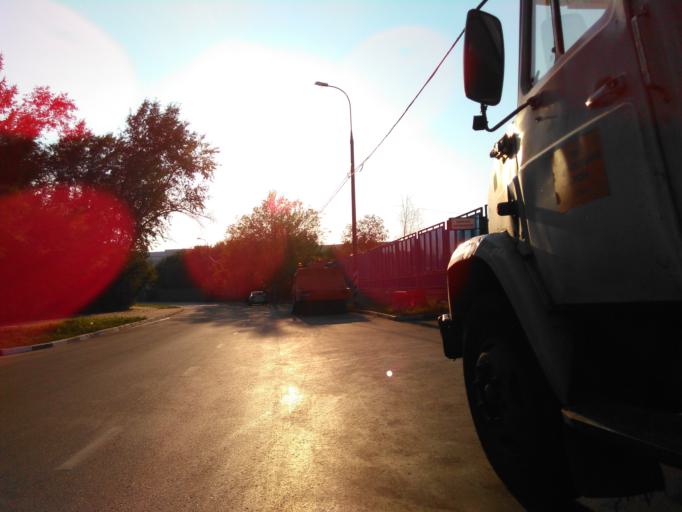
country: RU
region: Moskovskaya
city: Cheremushki
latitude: 55.6579
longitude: 37.5517
